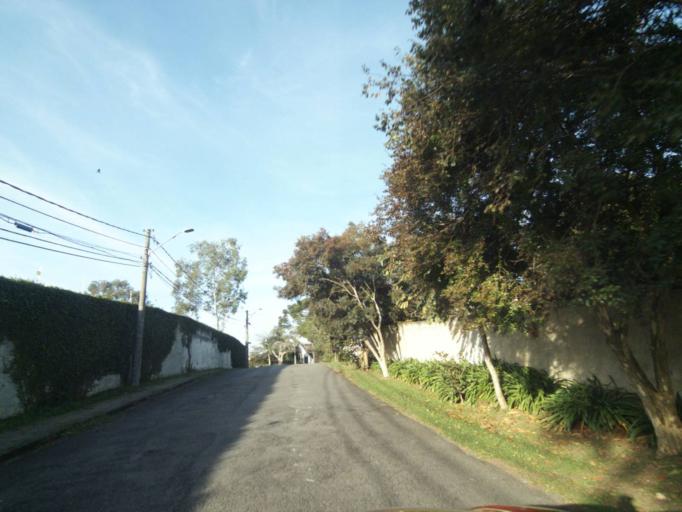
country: BR
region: Parana
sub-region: Curitiba
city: Curitiba
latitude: -25.4289
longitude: -49.3016
